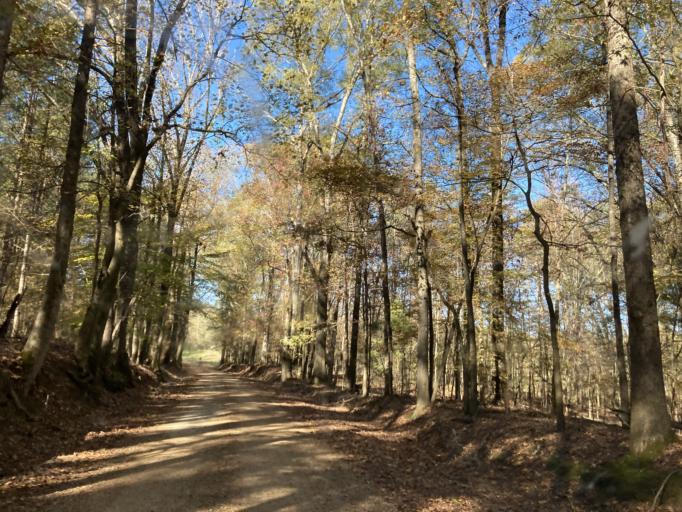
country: US
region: Mississippi
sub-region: Hinds County
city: Lynchburg
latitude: 32.5521
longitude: -90.4979
